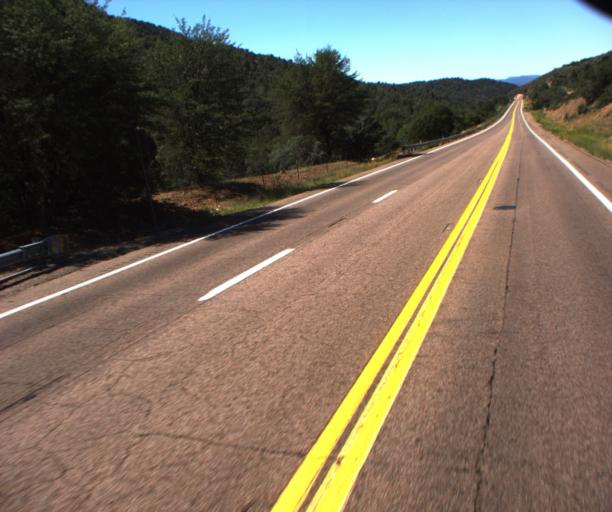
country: US
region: Arizona
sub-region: Navajo County
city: Cibecue
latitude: 33.8847
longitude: -110.3893
